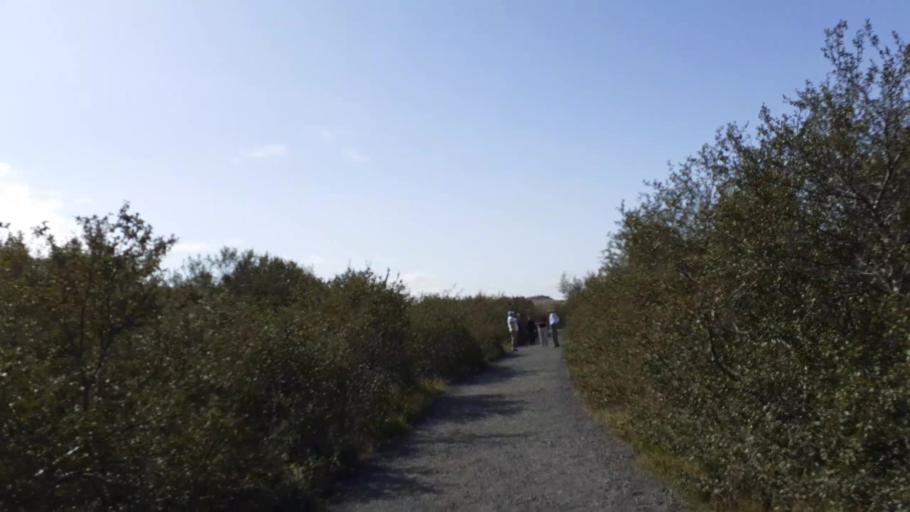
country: IS
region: West
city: Borgarnes
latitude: 64.7545
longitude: -21.5478
